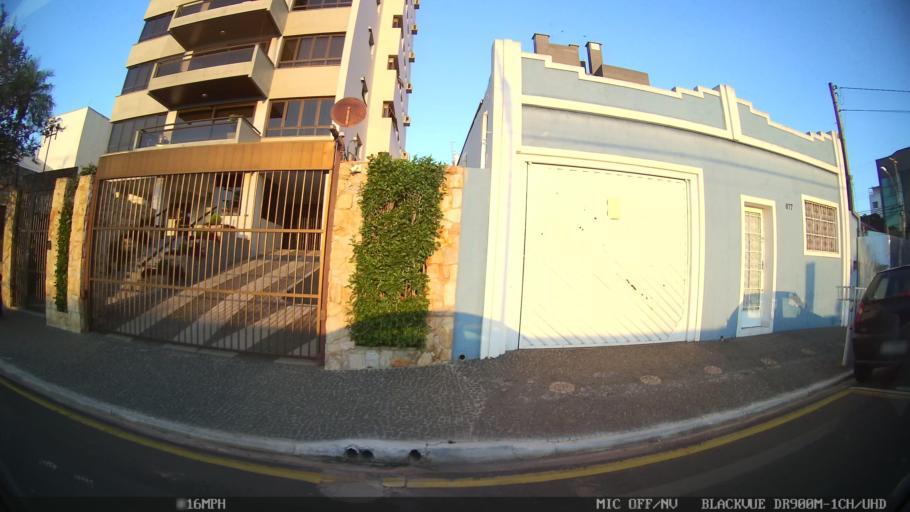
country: BR
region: Sao Paulo
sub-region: Santa Barbara D'Oeste
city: Santa Barbara d'Oeste
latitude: -22.7547
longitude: -47.4155
